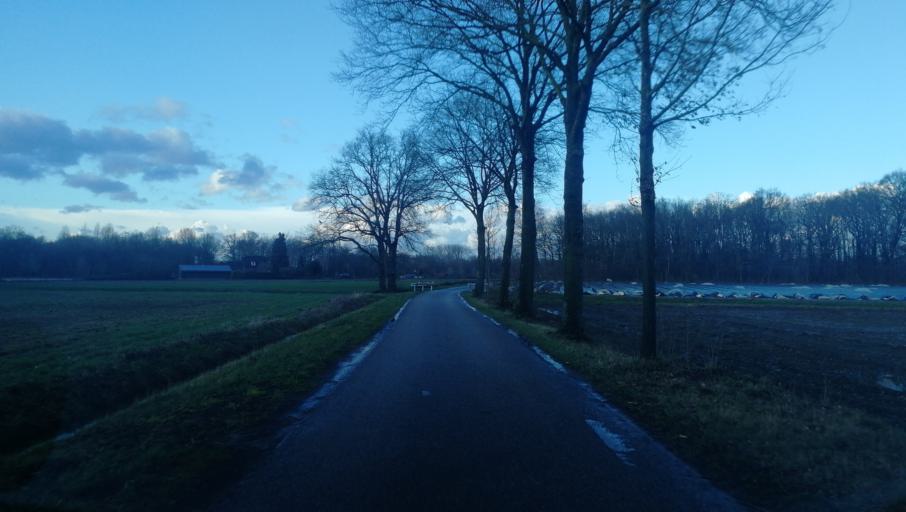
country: NL
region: Limburg
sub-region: Gemeente Peel en Maas
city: Maasbree
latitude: 51.3418
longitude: 6.0332
